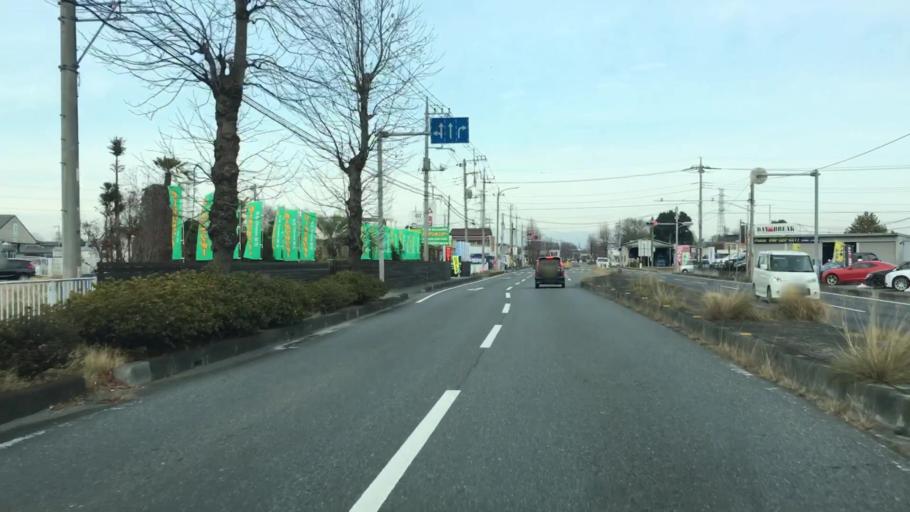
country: JP
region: Saitama
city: Kumagaya
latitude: 36.1759
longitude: 139.3701
